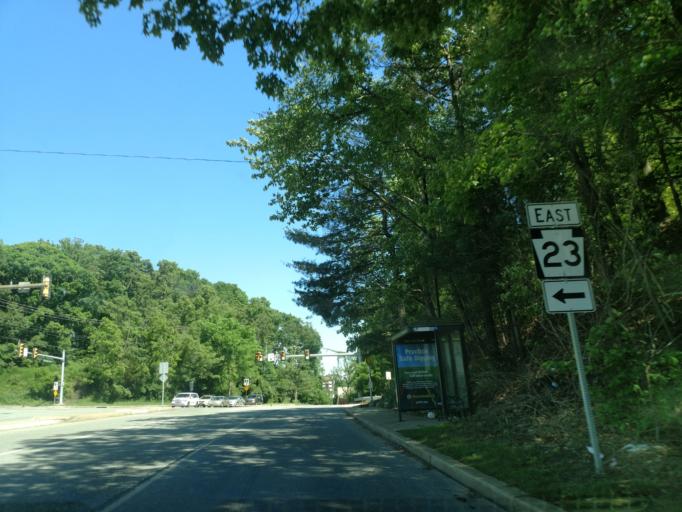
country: US
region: Pennsylvania
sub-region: Montgomery County
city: King of Prussia
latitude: 40.1033
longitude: -75.4013
